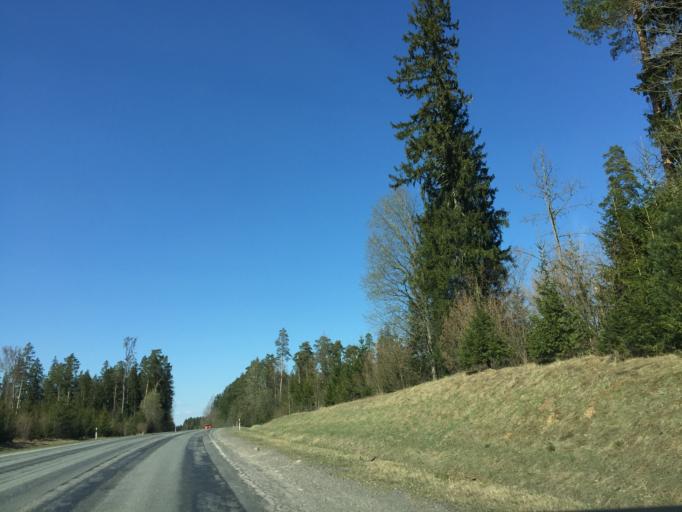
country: EE
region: Viljandimaa
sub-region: Viljandi linn
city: Viljandi
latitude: 58.2879
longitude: 25.5824
